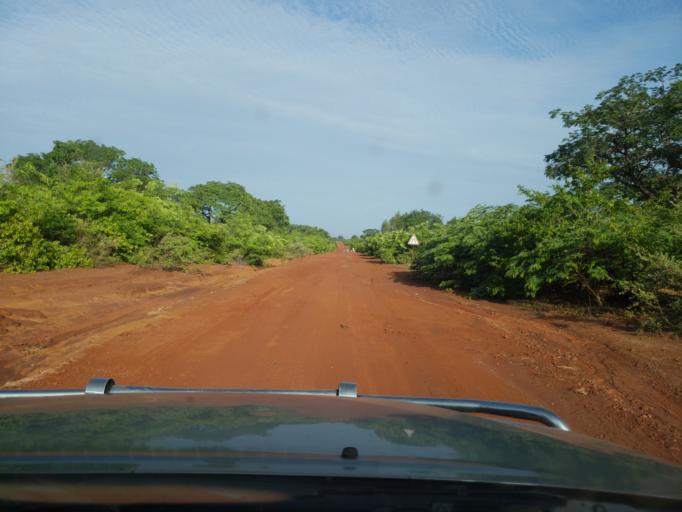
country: ML
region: Sikasso
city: Koutiala
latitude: 12.4242
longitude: -5.6638
